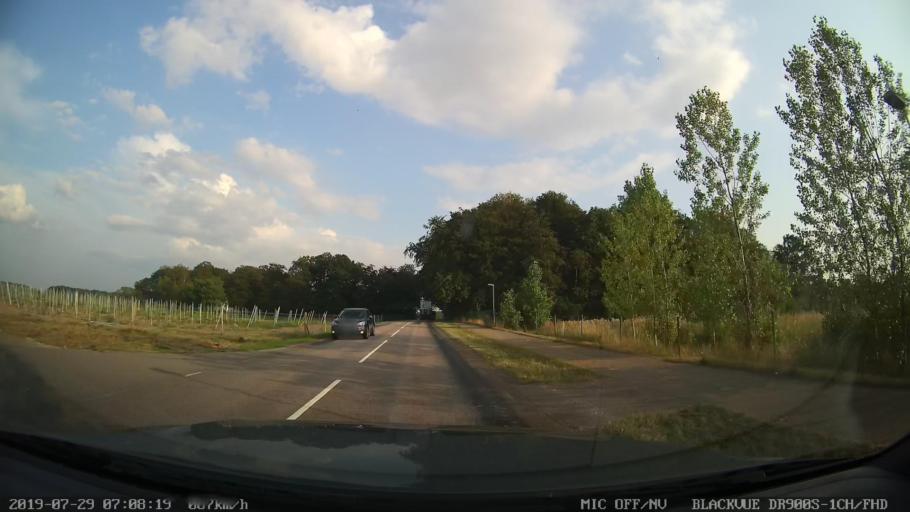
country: SE
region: Skane
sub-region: Helsingborg
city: Odakra
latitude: 56.1002
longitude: 12.6982
